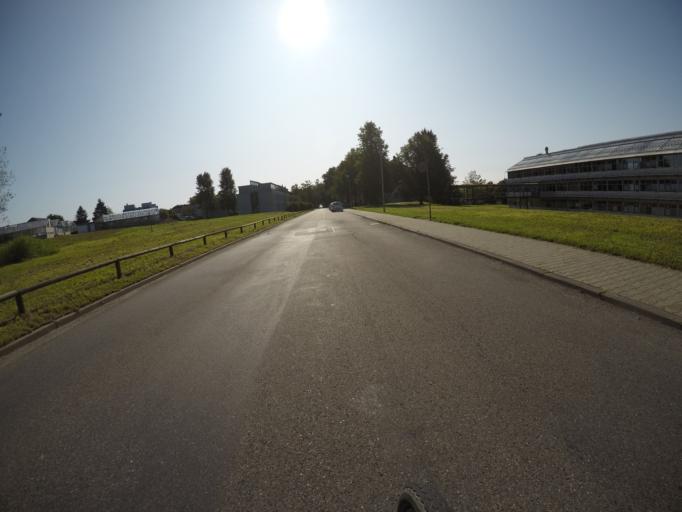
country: DE
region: Baden-Wuerttemberg
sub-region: Regierungsbezirk Stuttgart
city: Leinfelden-Echterdingen
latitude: 48.7137
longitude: 9.2070
